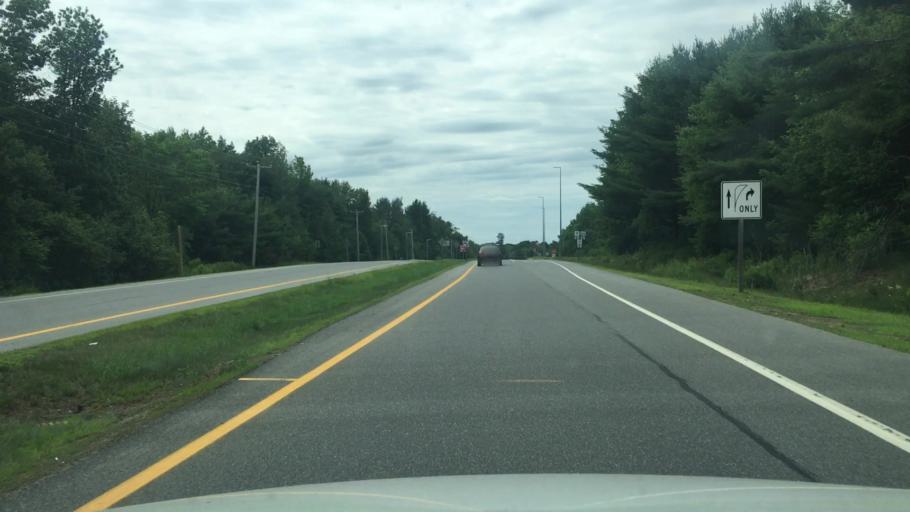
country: US
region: Maine
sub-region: Kennebec County
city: Windsor
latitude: 44.3978
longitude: -69.5655
